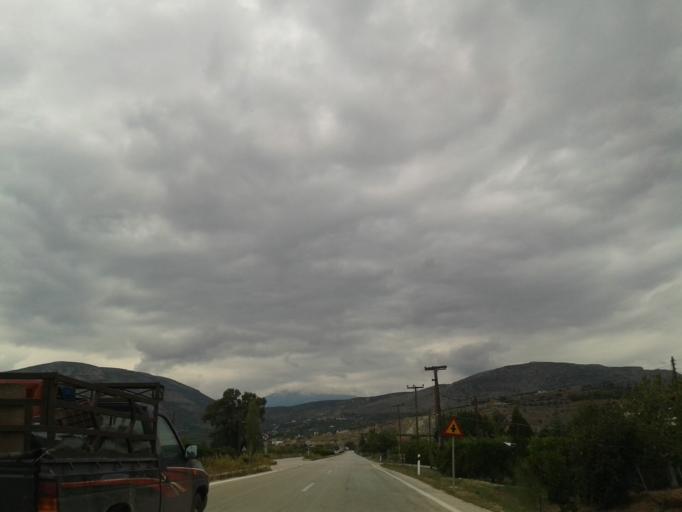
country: GR
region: Peloponnese
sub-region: Nomos Argolidos
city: Argos
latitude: 37.6153
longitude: 22.7197
